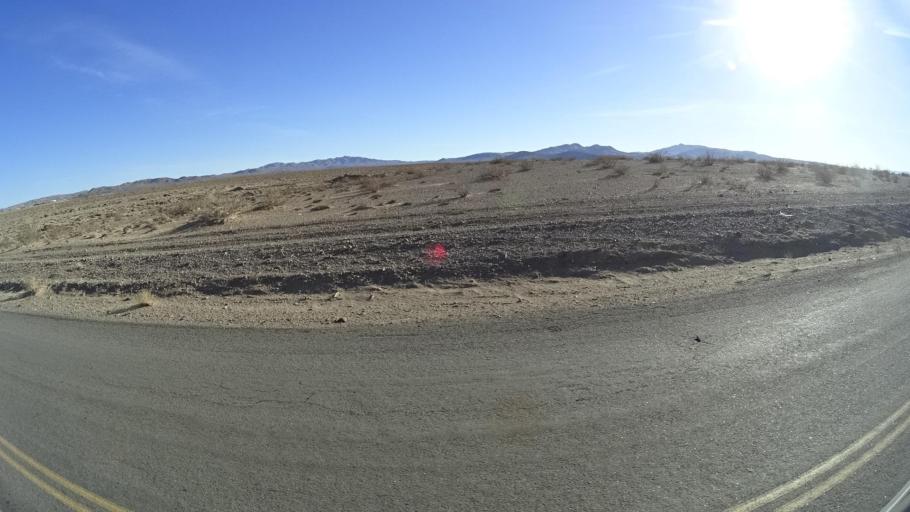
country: US
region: California
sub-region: Kern County
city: China Lake Acres
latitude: 35.6077
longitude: -117.7537
